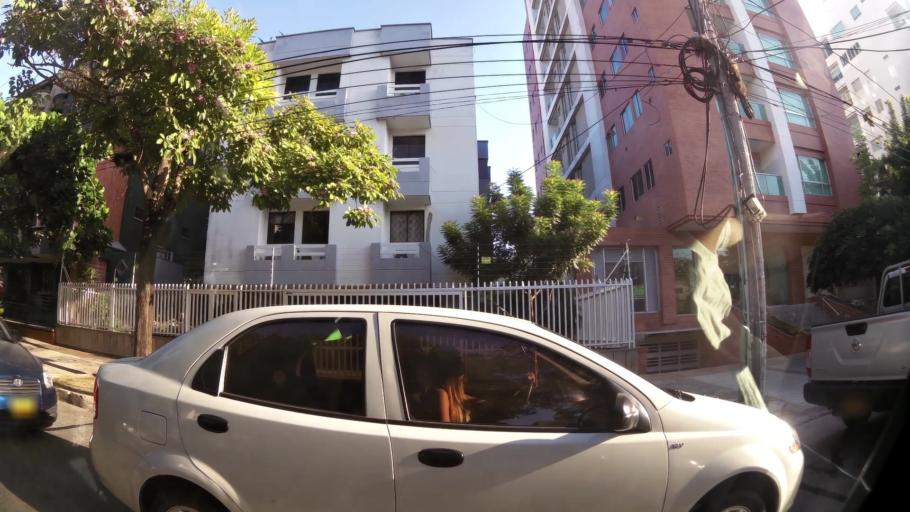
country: CO
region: Atlantico
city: Barranquilla
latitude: 11.0075
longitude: -74.8188
